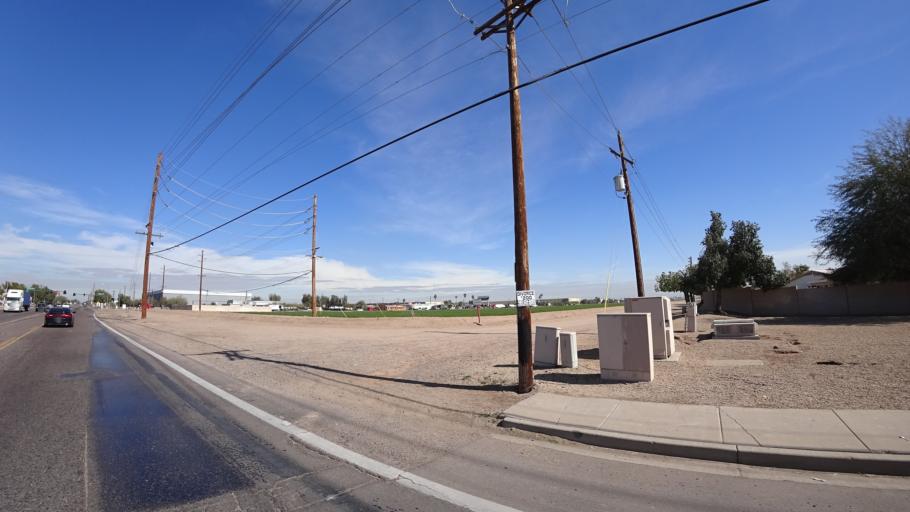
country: US
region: Arizona
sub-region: Maricopa County
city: Tolleson
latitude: 33.4353
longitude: -112.2037
